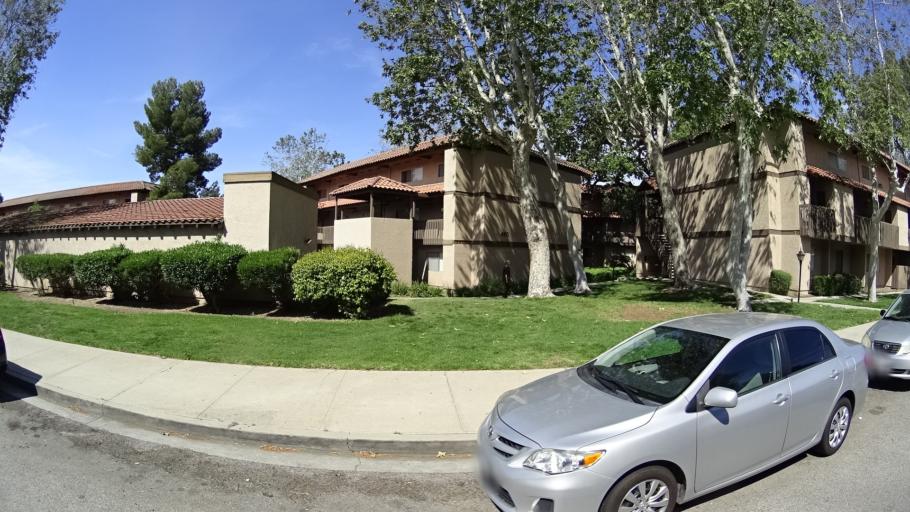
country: US
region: California
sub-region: Ventura County
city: Thousand Oaks
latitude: 34.1851
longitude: -118.8684
